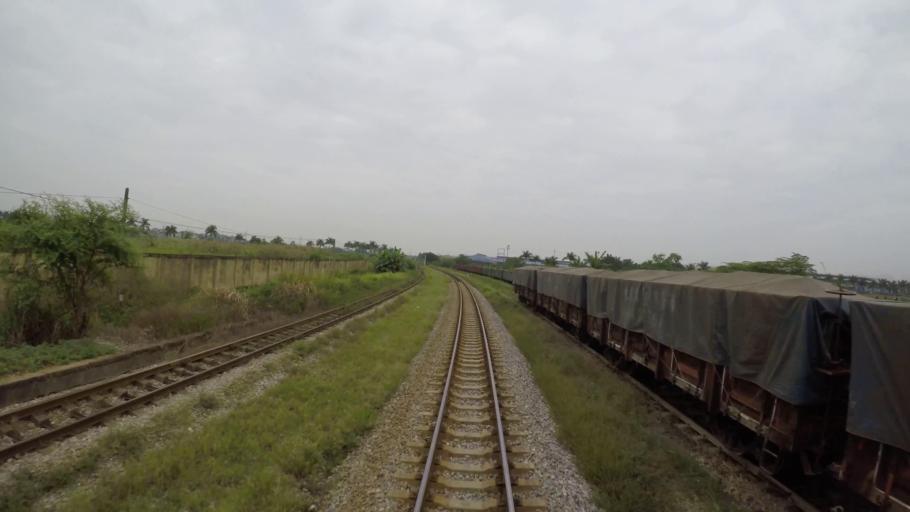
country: VN
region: Hai Phong
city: An Duong
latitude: 20.9056
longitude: 106.5748
